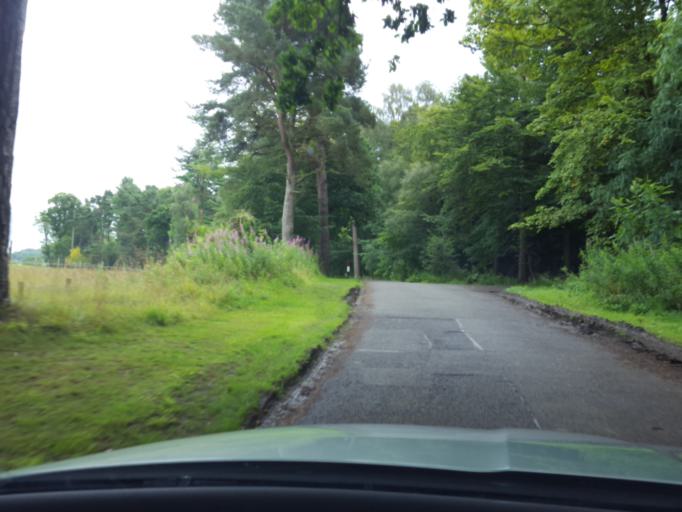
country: GB
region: Scotland
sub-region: Falkirk
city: Polmont
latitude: 55.9615
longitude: -3.6654
